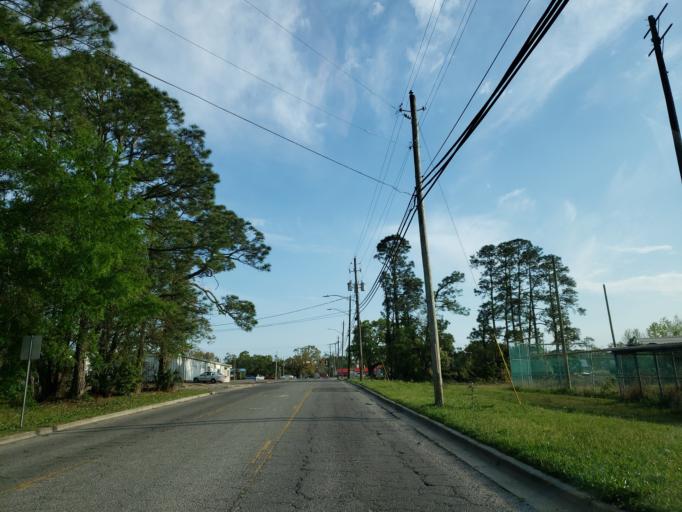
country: US
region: Mississippi
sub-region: Harrison County
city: West Gulfport
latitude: 30.3909
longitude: -89.0610
